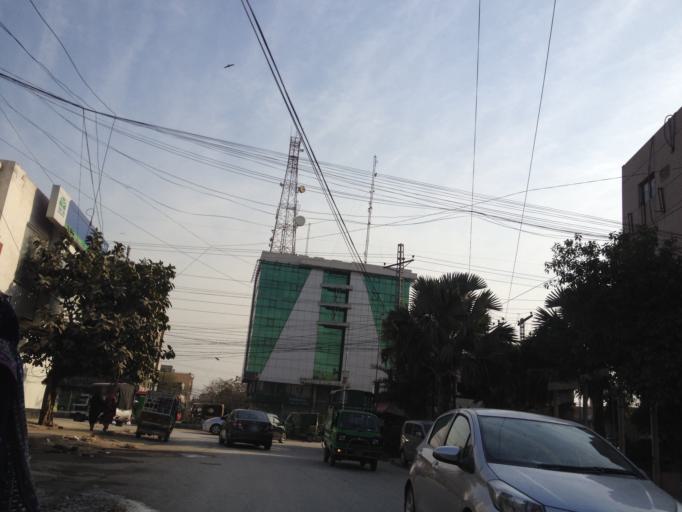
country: PK
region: Punjab
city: Lahore
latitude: 31.5023
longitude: 74.3192
